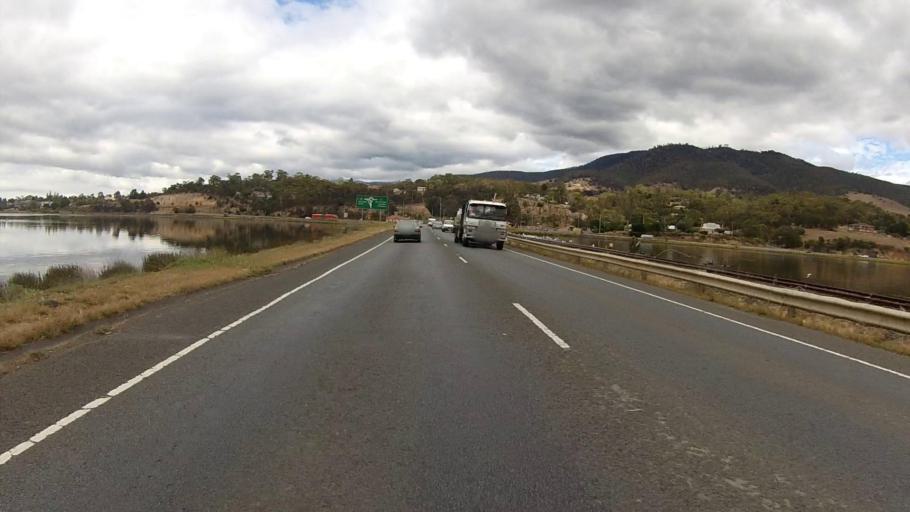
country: AU
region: Tasmania
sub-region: Glenorchy
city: Granton
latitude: -42.7463
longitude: 147.2248
